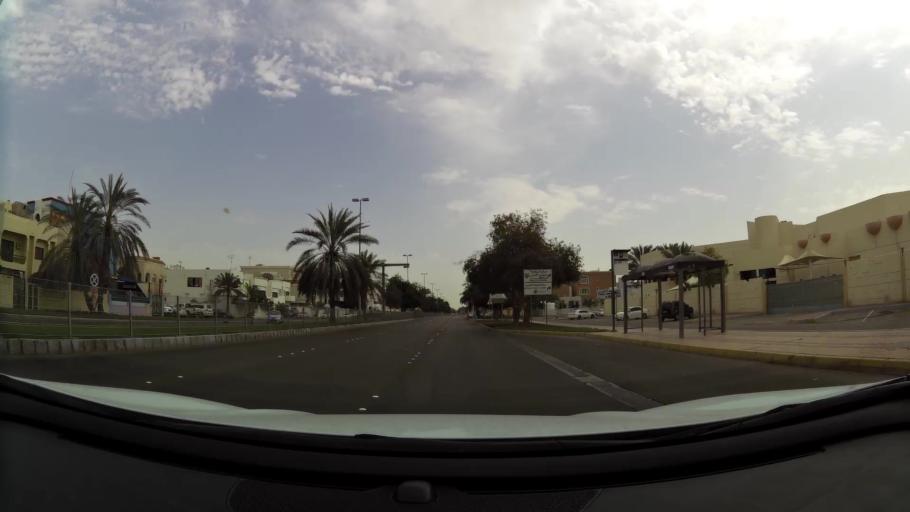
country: AE
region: Abu Dhabi
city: Abu Dhabi
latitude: 24.4643
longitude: 54.3675
